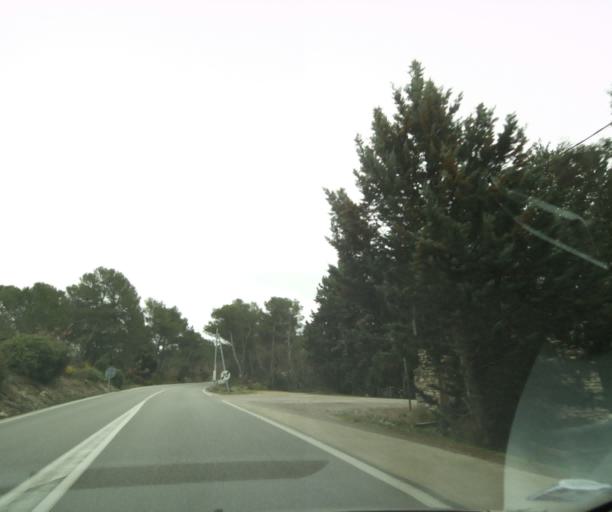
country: FR
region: Provence-Alpes-Cote d'Azur
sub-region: Departement des Bouches-du-Rhone
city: Greasque
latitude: 43.4351
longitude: 5.5604
